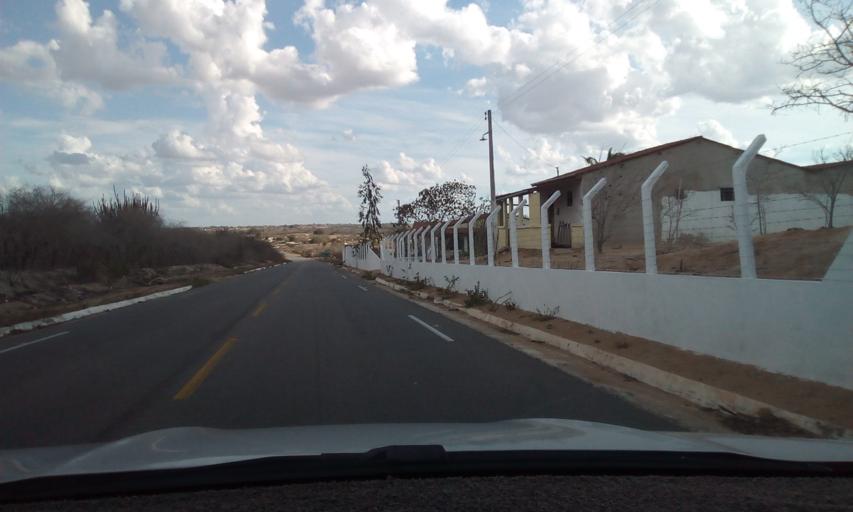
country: BR
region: Paraiba
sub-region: Soledade
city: Soledade
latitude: -6.8874
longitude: -36.3987
